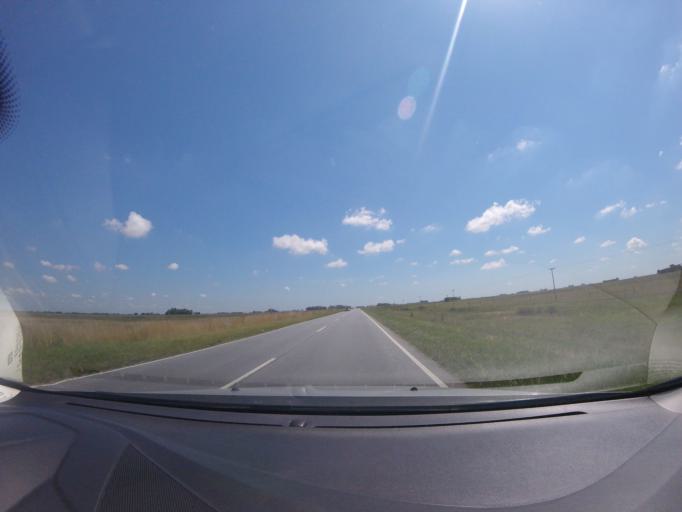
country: AR
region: Buenos Aires
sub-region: Partido de Rauch
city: Rauch
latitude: -36.8778
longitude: -58.9902
